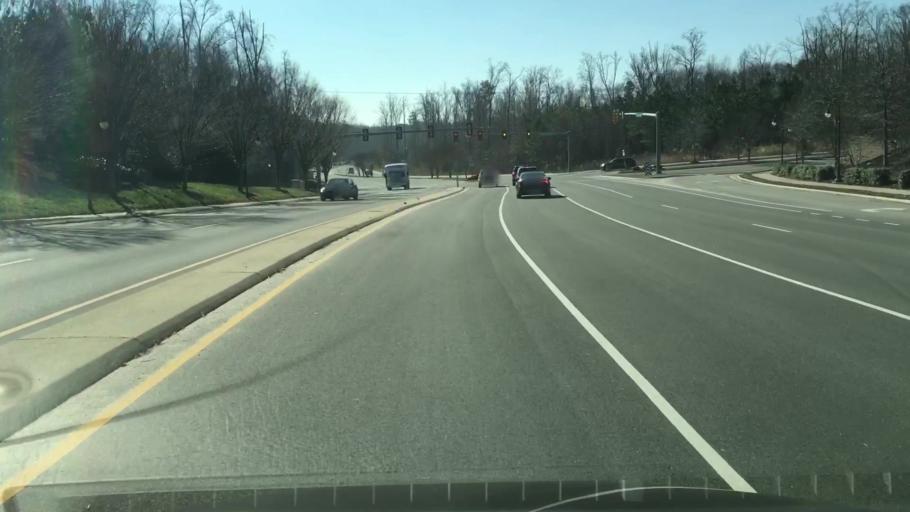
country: US
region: Virginia
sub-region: Chesterfield County
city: Brandermill
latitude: 37.5004
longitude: -77.6409
